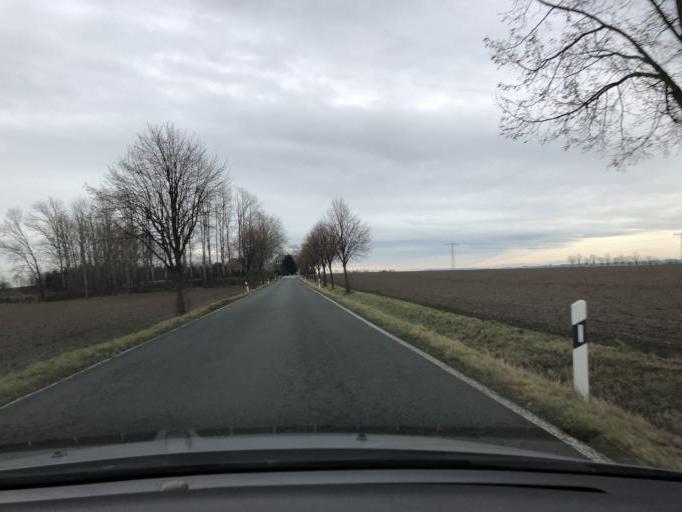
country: DE
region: Saxony
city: Nossen
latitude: 51.0693
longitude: 13.3175
